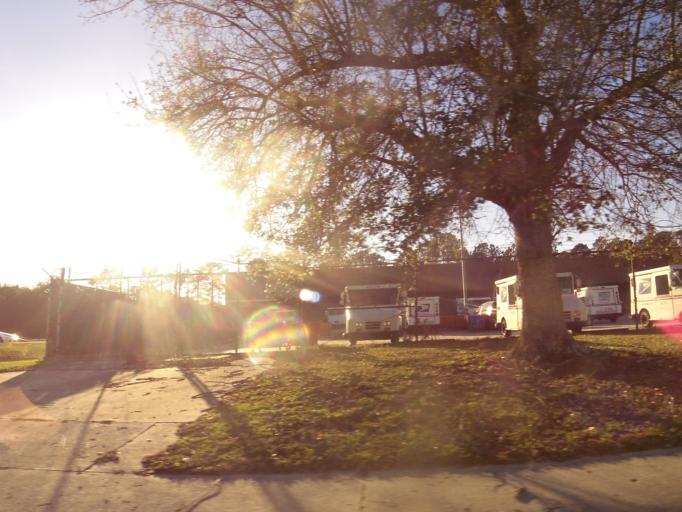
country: US
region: Florida
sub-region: Saint Johns County
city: Fruit Cove
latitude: 30.2069
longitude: -81.6003
